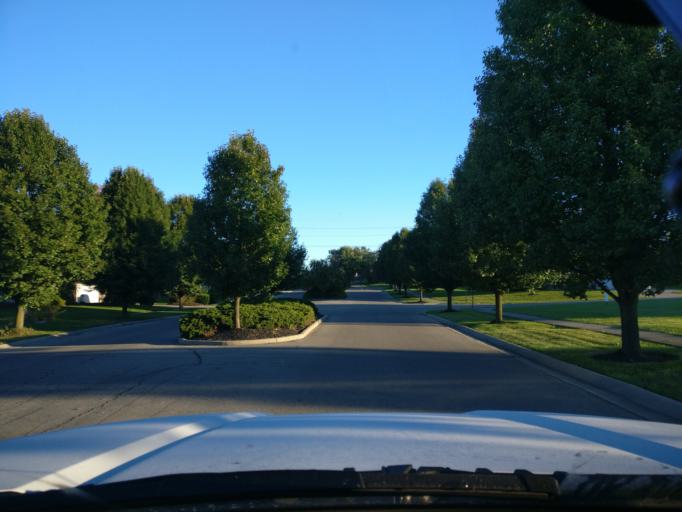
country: US
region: Ohio
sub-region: Warren County
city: Hunter
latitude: 39.4902
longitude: -84.2693
